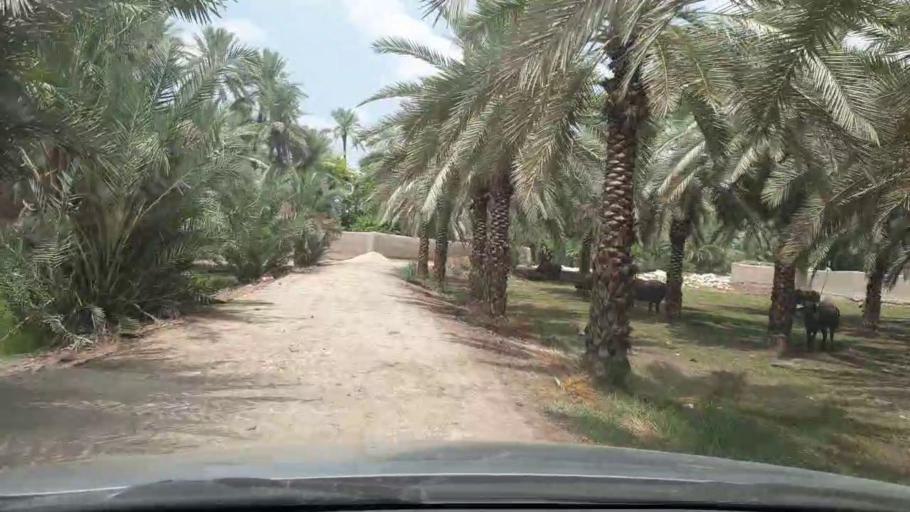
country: PK
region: Sindh
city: Kot Diji
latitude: 27.4211
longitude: 68.7646
